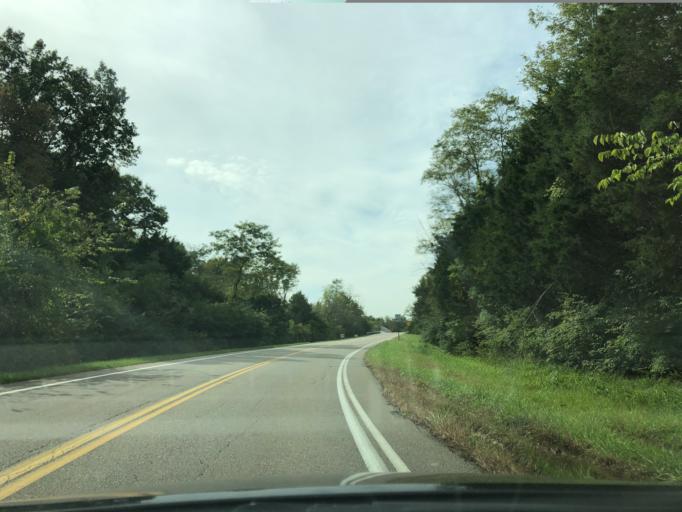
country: US
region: Ohio
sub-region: Hamilton County
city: The Village of Indian Hill
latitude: 39.2352
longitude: -84.2898
